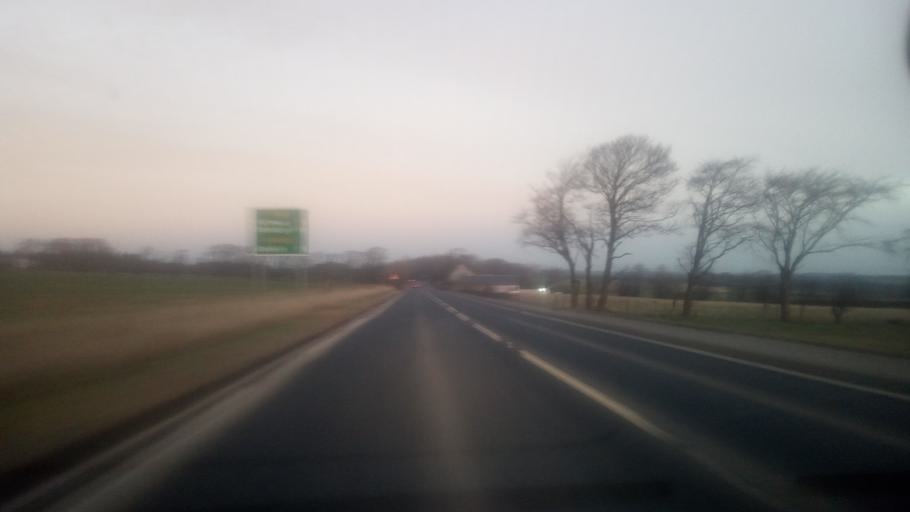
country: GB
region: Scotland
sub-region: East Lothian
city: Pencaitland
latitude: 55.8308
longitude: -2.8860
